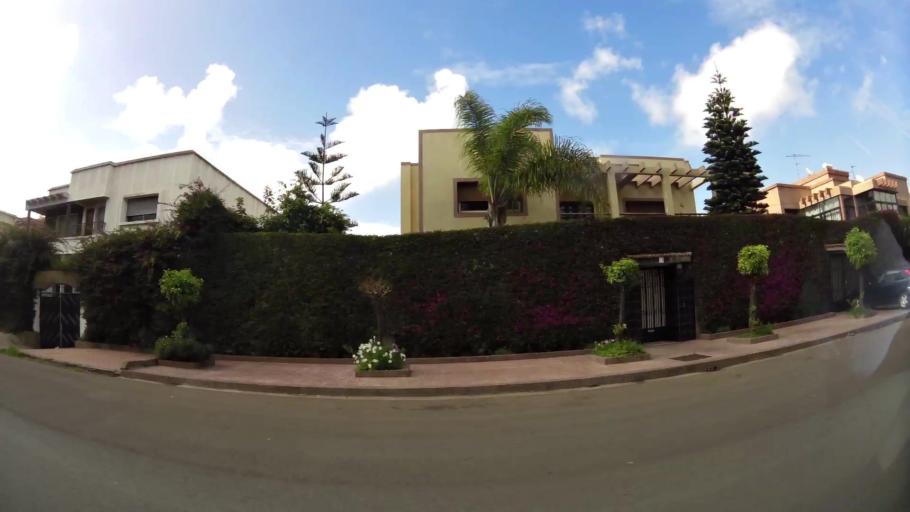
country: MA
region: Grand Casablanca
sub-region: Casablanca
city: Casablanca
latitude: 33.5520
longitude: -7.6272
